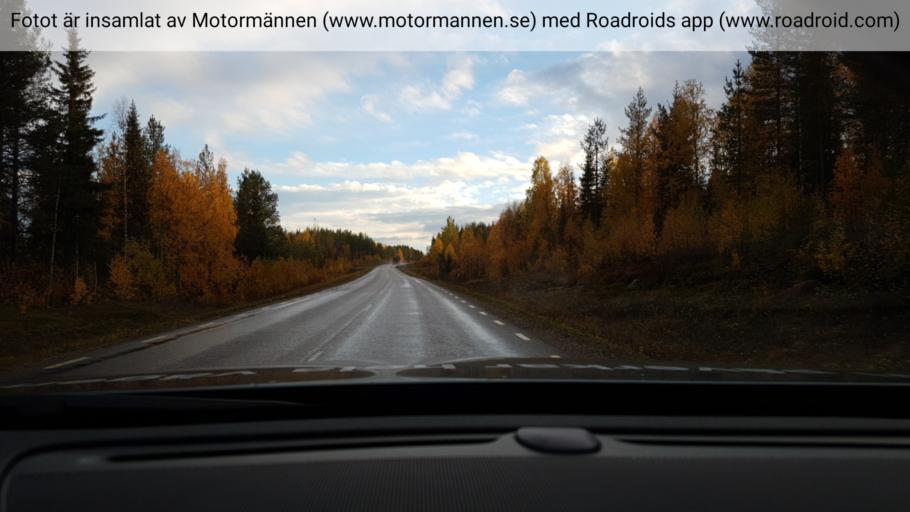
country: SE
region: Norrbotten
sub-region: Overkalix Kommun
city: OEverkalix
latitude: 66.7441
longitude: 22.6702
